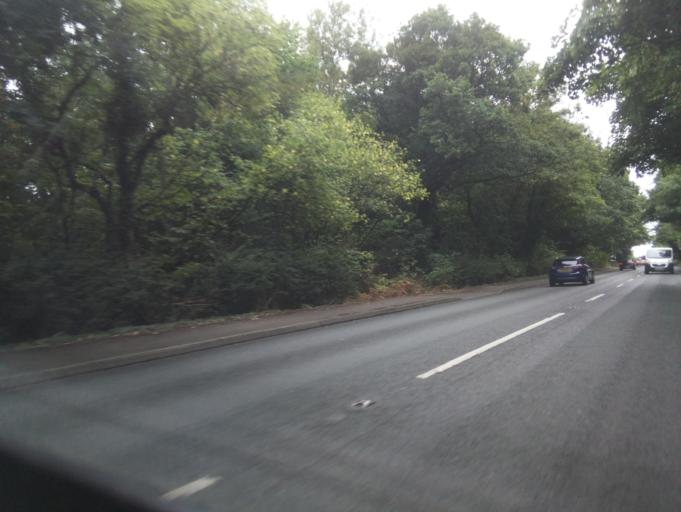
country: GB
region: England
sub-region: Kirklees
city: Clayton West
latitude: 53.6175
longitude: -1.5920
